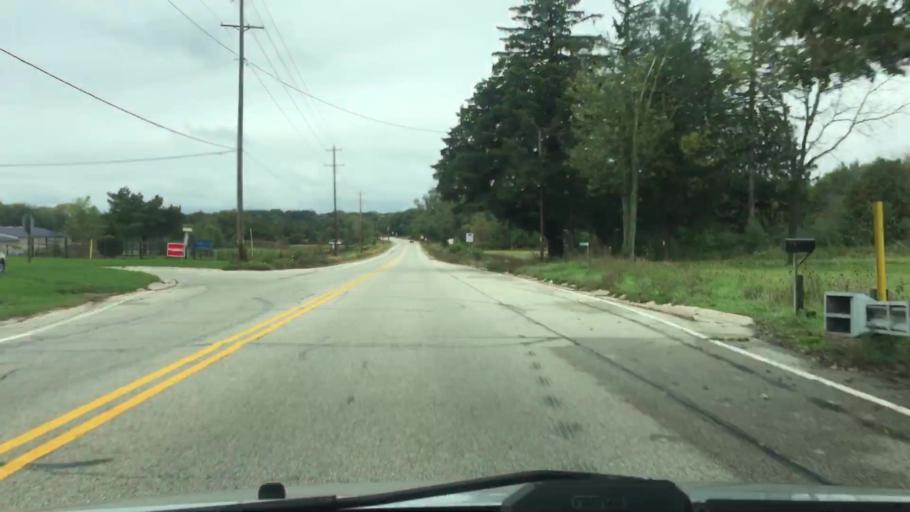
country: US
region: Wisconsin
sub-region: Waukesha County
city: Eagle
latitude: 42.8574
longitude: -88.4949
